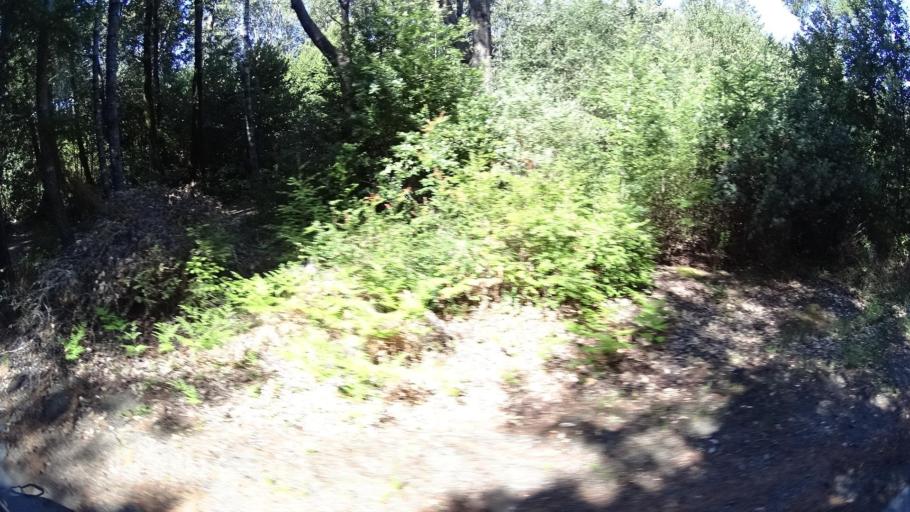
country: US
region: California
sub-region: Humboldt County
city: Redway
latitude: 40.2046
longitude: -124.1030
